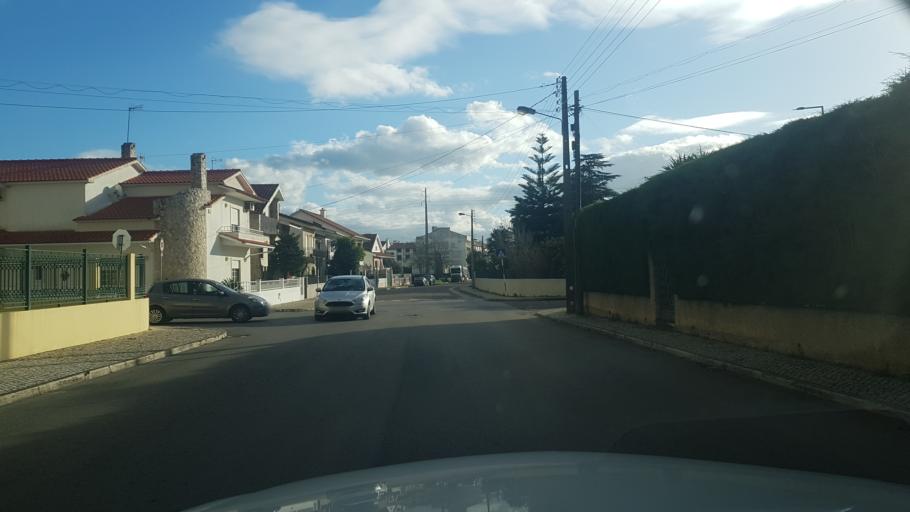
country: PT
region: Santarem
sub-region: Entroncamento
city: Entroncamento
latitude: 39.4731
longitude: -8.4730
